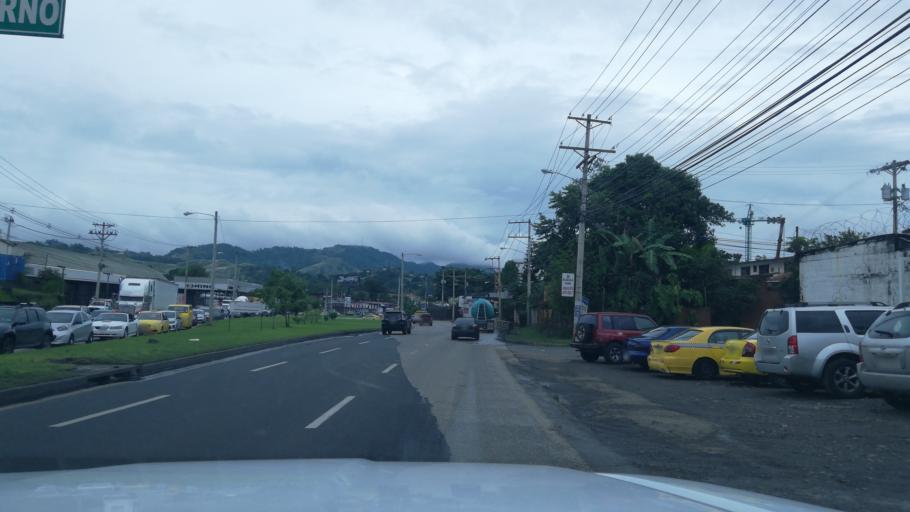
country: PA
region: Panama
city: Las Cumbres
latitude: 9.0703
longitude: -79.5201
